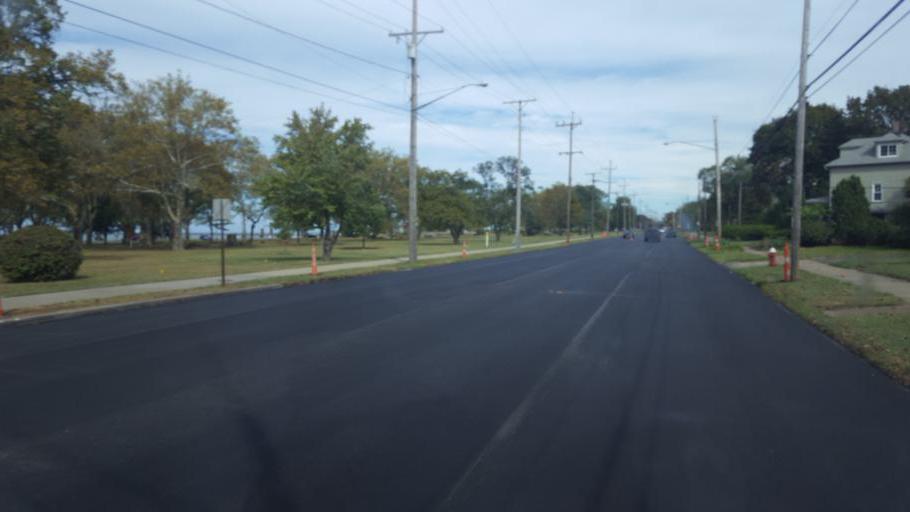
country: US
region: Ohio
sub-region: Lorain County
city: Lorain
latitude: 41.4611
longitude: -82.1972
